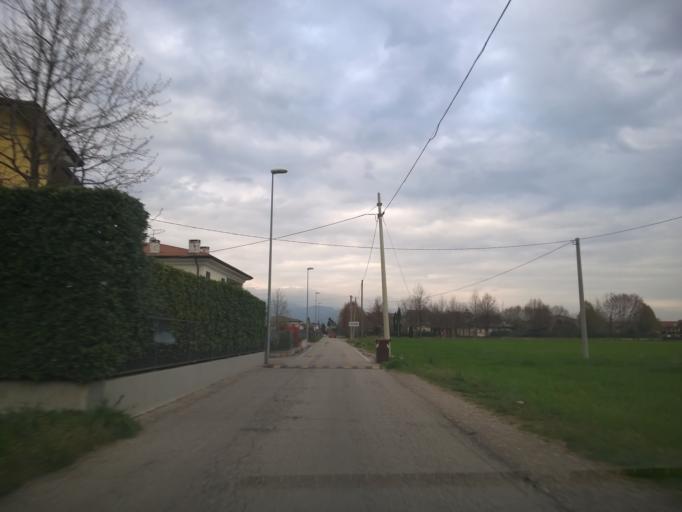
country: IT
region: Veneto
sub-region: Provincia di Vicenza
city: Thiene
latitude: 45.6950
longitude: 11.4726
